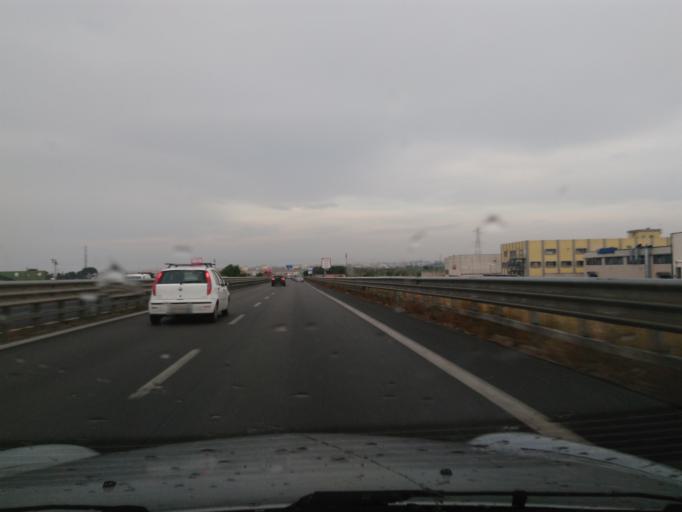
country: IT
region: Apulia
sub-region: Provincia di Bari
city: Molfetta
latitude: 41.2048
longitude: 16.5658
